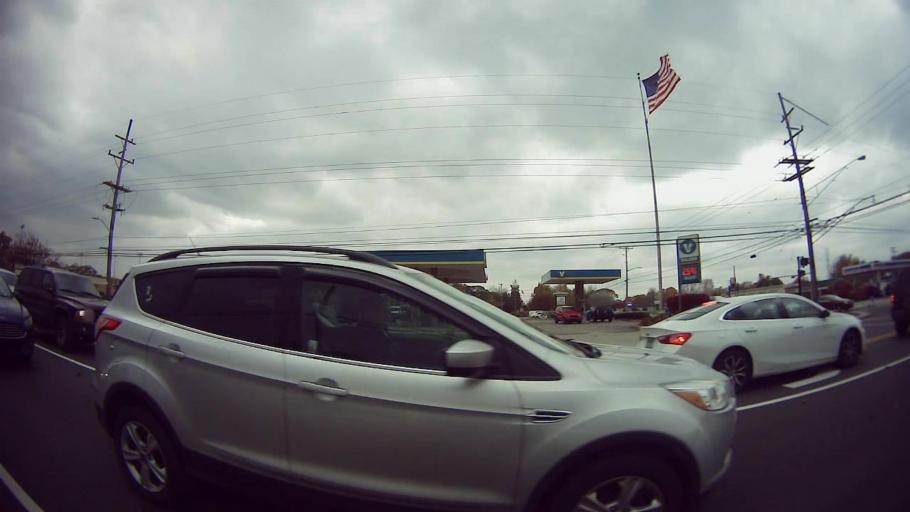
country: US
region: Michigan
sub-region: Macomb County
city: Center Line
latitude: 42.5211
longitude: -83.0075
